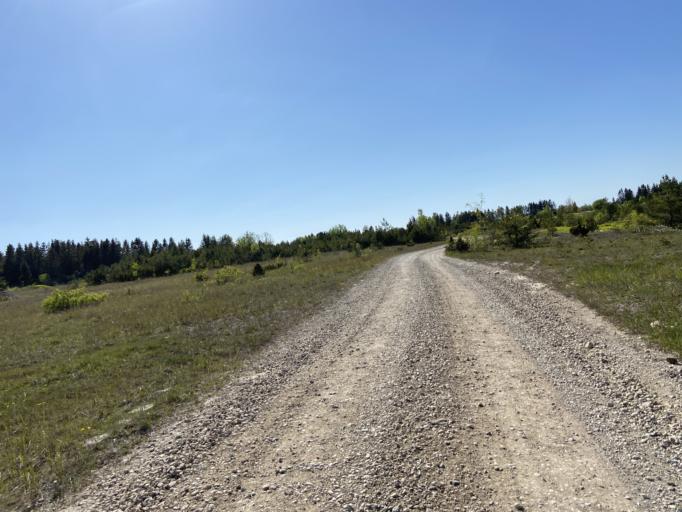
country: EE
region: Harju
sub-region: Paldiski linn
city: Paldiski
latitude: 59.2679
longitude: 23.7429
